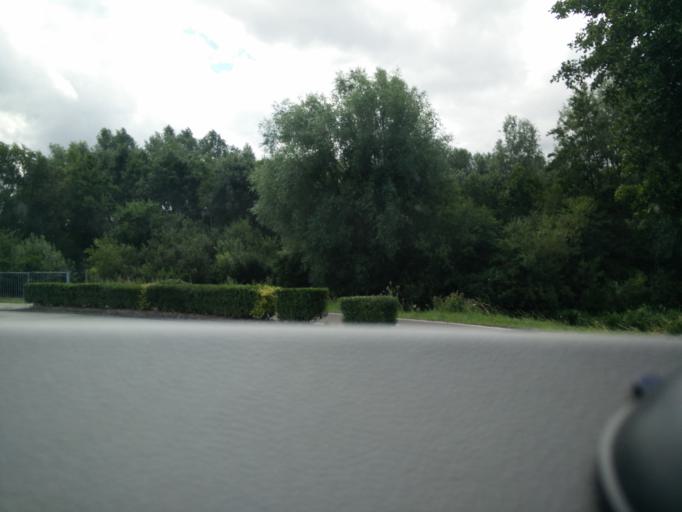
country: FR
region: Nord-Pas-de-Calais
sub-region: Departement du Nord
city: Bergues
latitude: 50.9734
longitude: 2.4233
